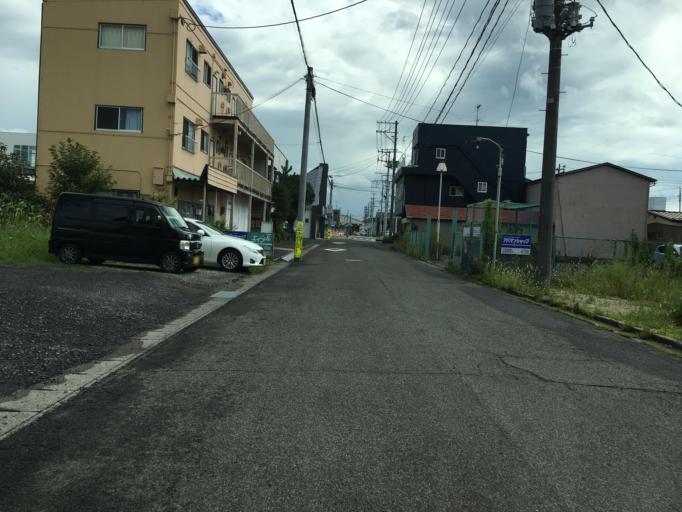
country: JP
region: Fukushima
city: Motomiya
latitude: 37.5150
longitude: 140.3987
